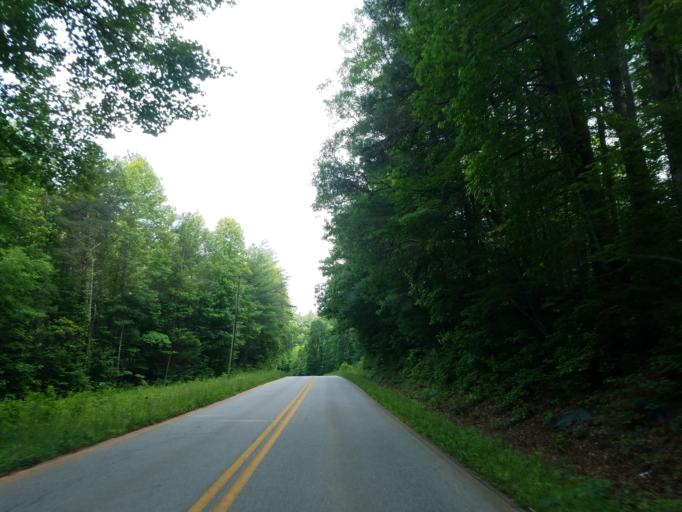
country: US
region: Georgia
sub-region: Lumpkin County
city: Dahlonega
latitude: 34.6169
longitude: -84.0741
